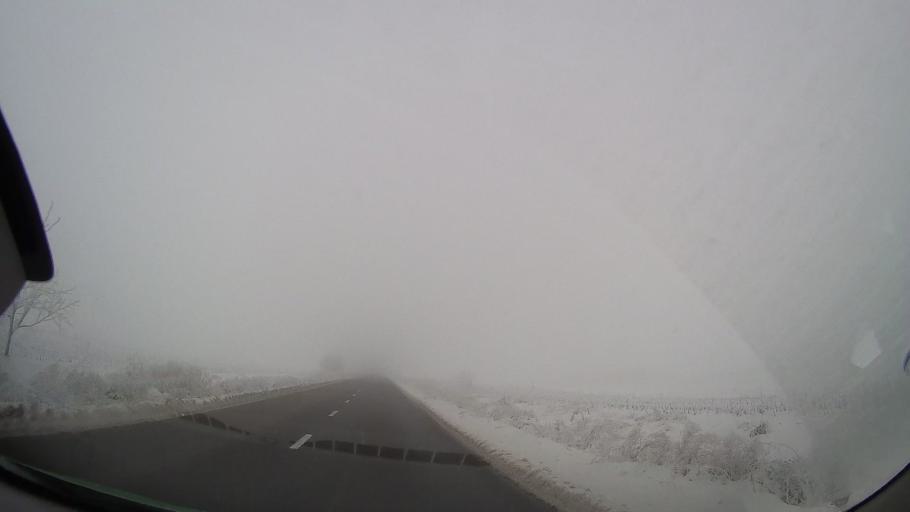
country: RO
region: Neamt
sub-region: Comuna Sabaoani
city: Sabaoani
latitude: 47.0373
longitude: 26.8536
